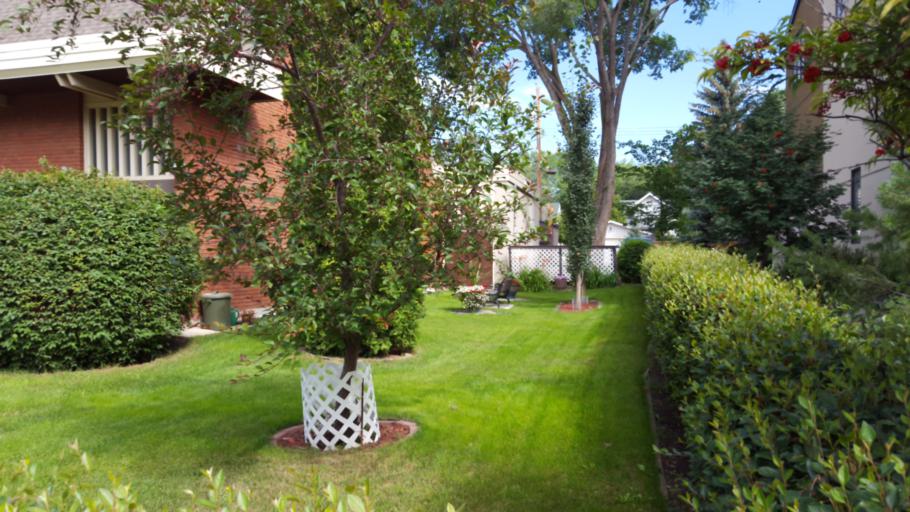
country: CA
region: Alberta
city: Edmonton
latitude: 53.5123
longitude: -113.5306
